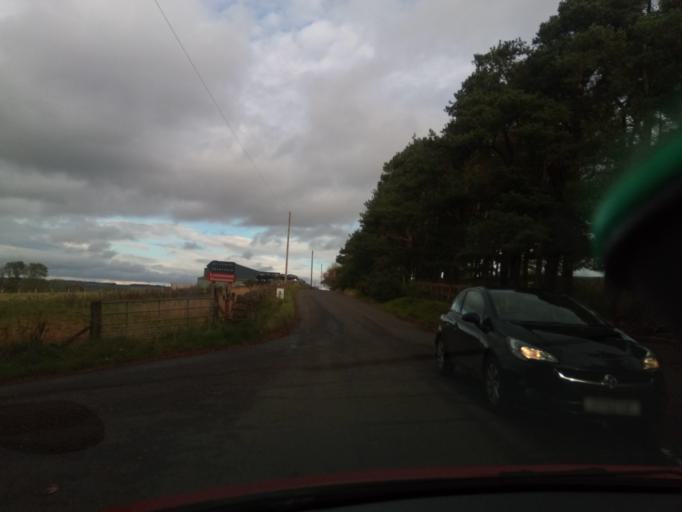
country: GB
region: Scotland
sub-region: South Lanarkshire
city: Carnwath
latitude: 55.7457
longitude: -3.6054
